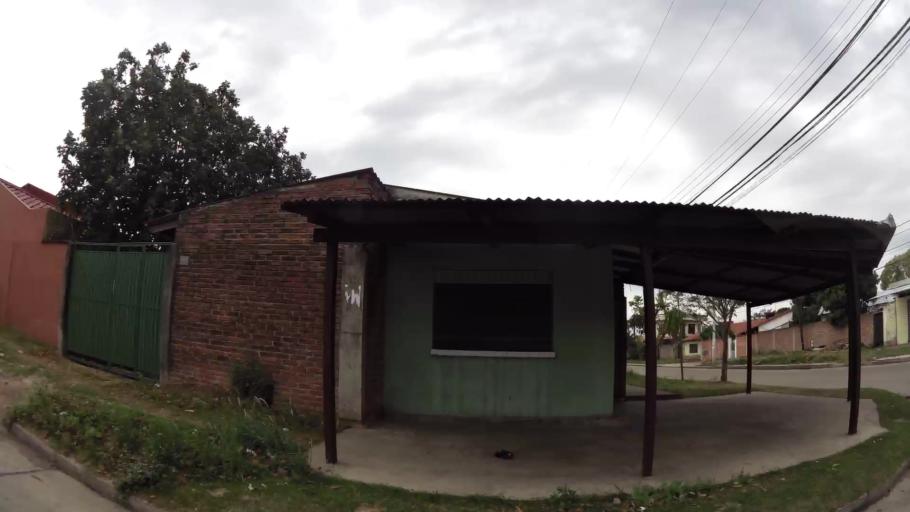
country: BO
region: Santa Cruz
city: Santa Cruz de la Sierra
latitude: -17.7760
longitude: -63.2133
